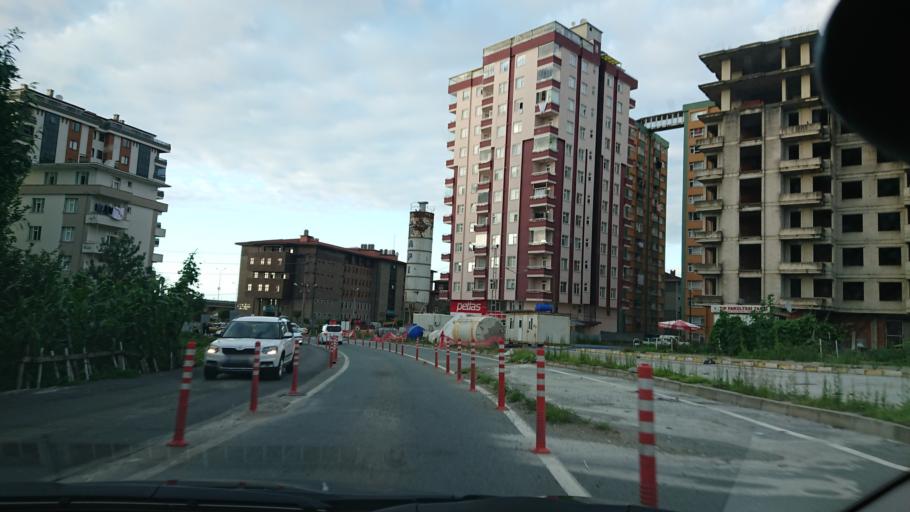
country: TR
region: Rize
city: Gundogdu
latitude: 41.0365
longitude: 40.5660
